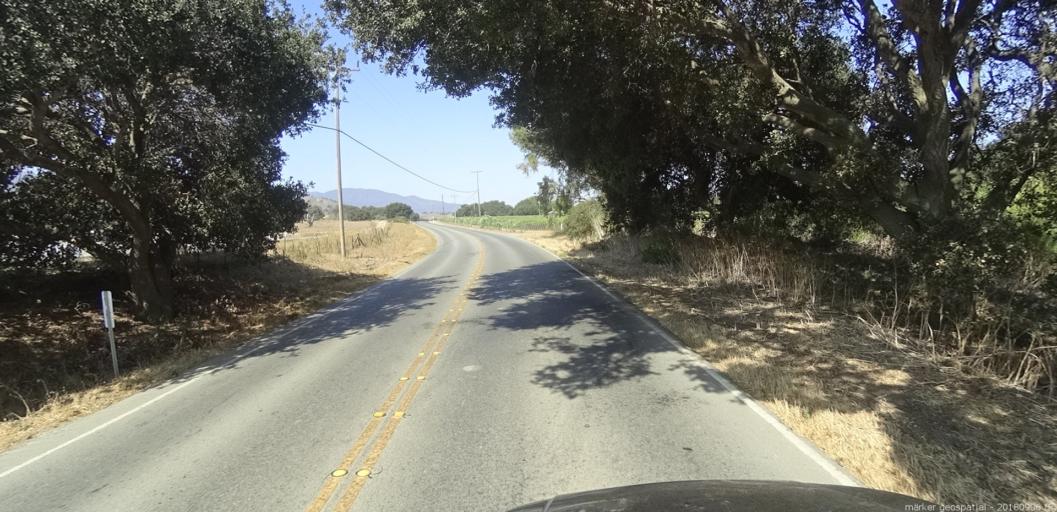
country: US
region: California
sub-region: Monterey County
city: Chualar
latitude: 36.5735
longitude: -121.5775
